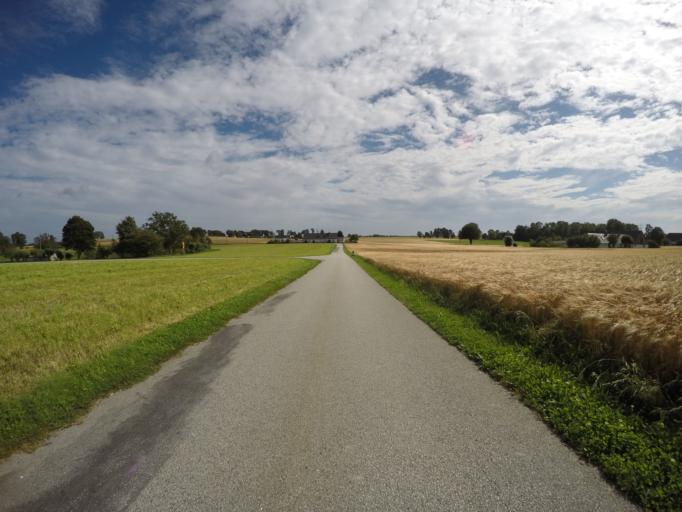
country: SE
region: Skane
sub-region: Simrishamns Kommun
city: Simrishamn
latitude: 55.4922
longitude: 14.2578
